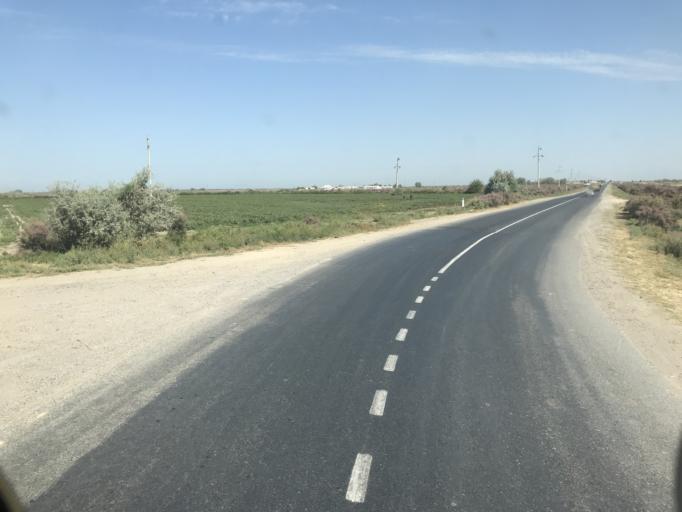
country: KZ
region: Ongtustik Qazaqstan
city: Myrzakent
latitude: 40.6802
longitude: 68.5322
